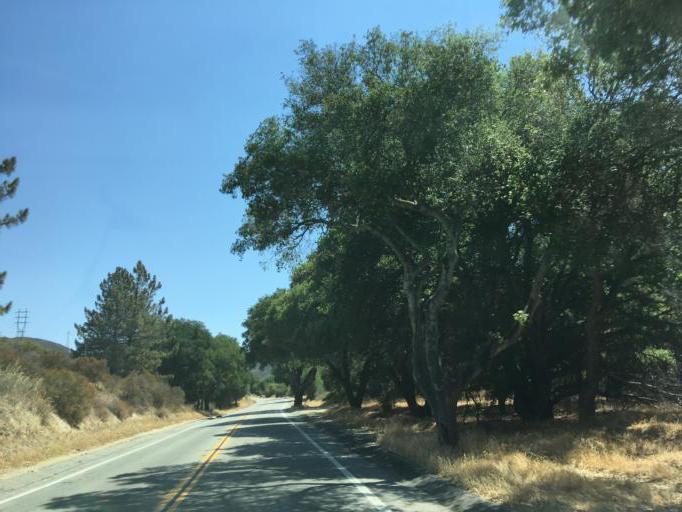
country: US
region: California
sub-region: Los Angeles County
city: Green Valley
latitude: 34.6303
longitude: -118.3976
